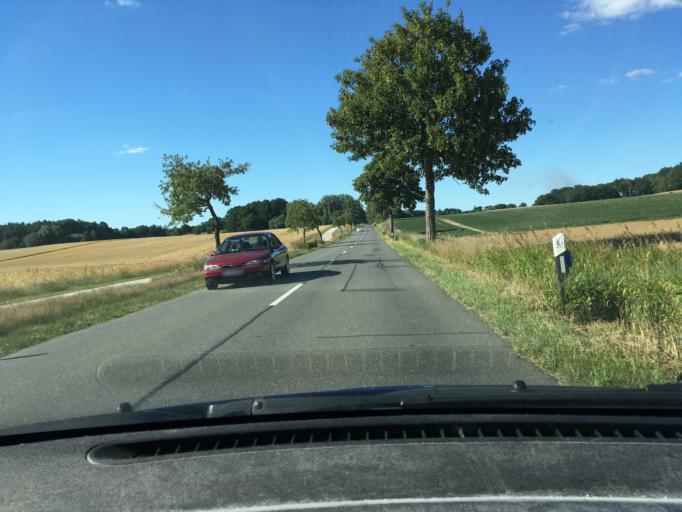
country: DE
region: Lower Saxony
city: Altenmedingen
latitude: 53.1818
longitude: 10.6300
